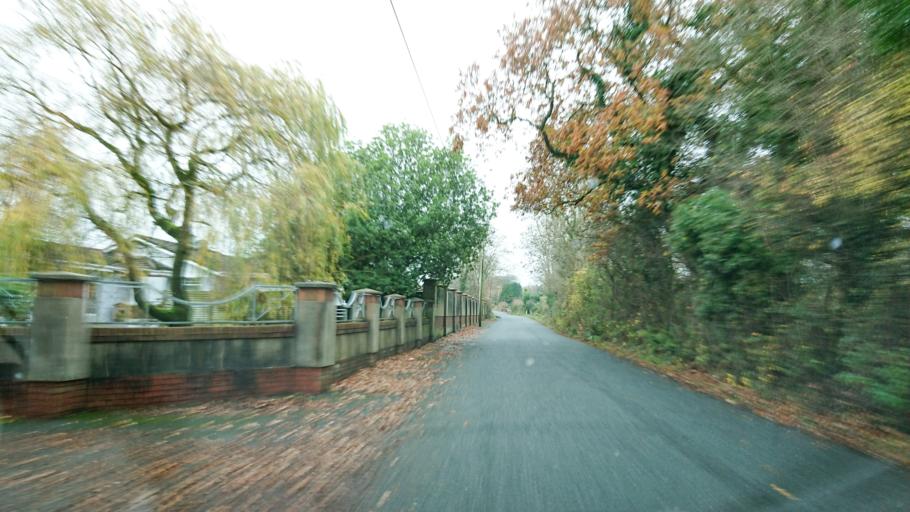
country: IE
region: Munster
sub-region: Waterford
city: Waterford
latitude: 52.2417
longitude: -7.1813
